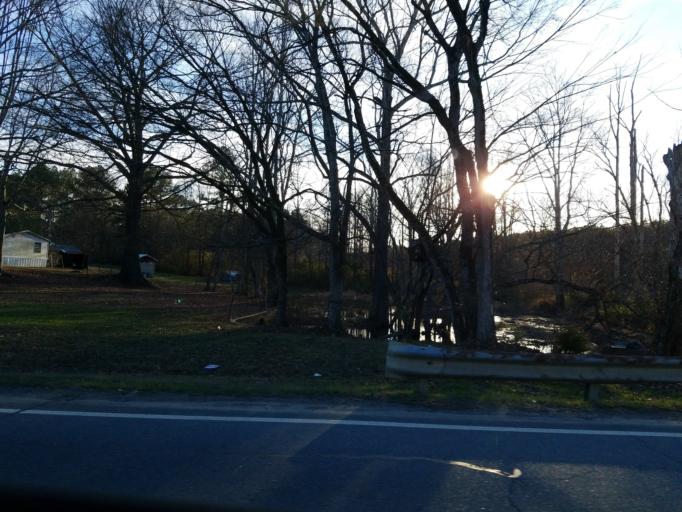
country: US
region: Georgia
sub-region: Whitfield County
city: Dalton
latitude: 34.6481
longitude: -84.9719
